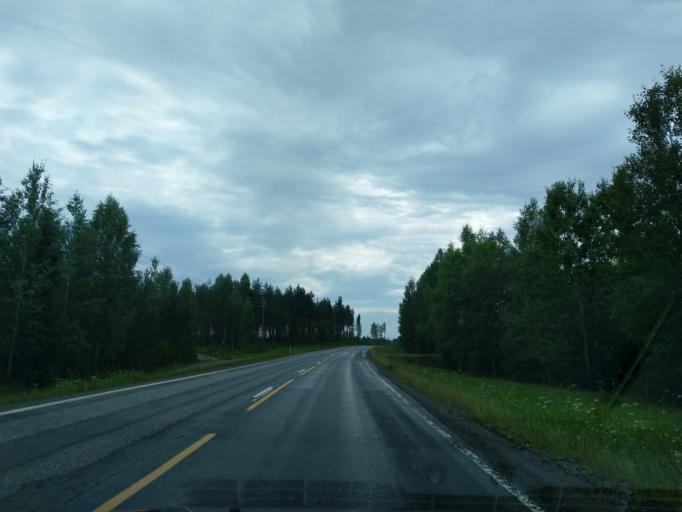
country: FI
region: Southern Savonia
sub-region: Savonlinna
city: Punkaharju
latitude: 61.6744
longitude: 29.4137
